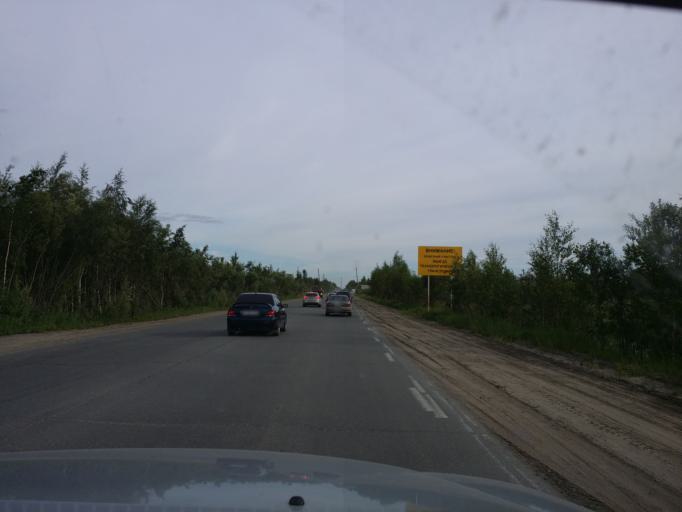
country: RU
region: Khanty-Mansiyskiy Avtonomnyy Okrug
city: Nizhnevartovsk
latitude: 60.9590
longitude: 76.6631
